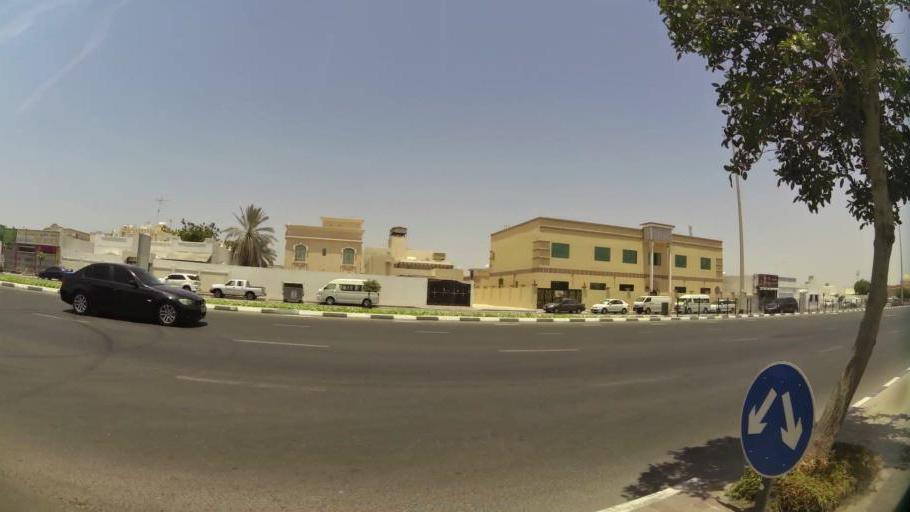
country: AE
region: Ash Shariqah
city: Sharjah
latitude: 25.2850
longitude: 55.3370
